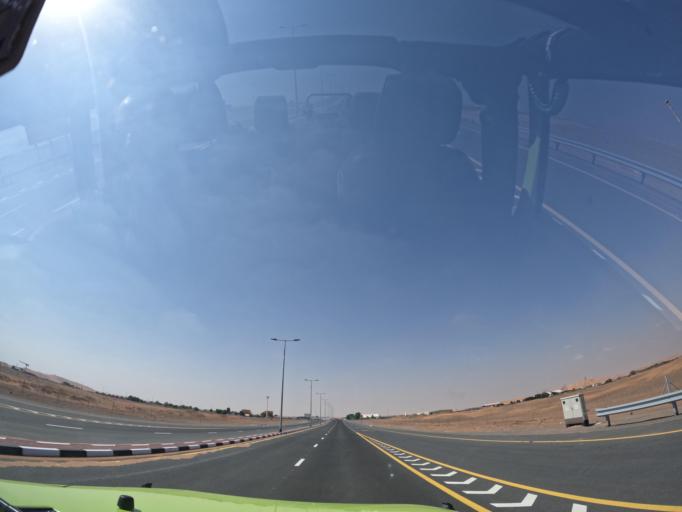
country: AE
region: Ash Shariqah
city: Adh Dhayd
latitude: 24.8126
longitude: 55.7991
